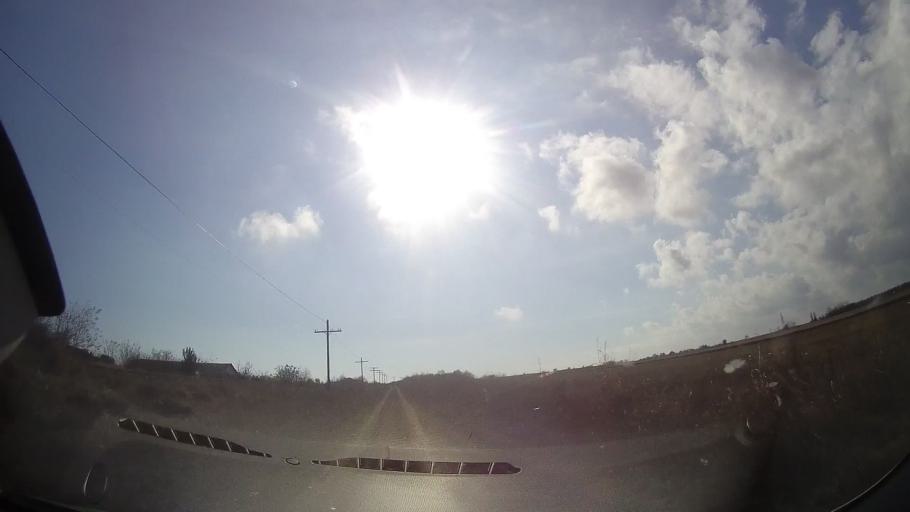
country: RO
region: Constanta
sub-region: Comuna Tuzla
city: Tuzla
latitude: 43.9919
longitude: 28.6451
